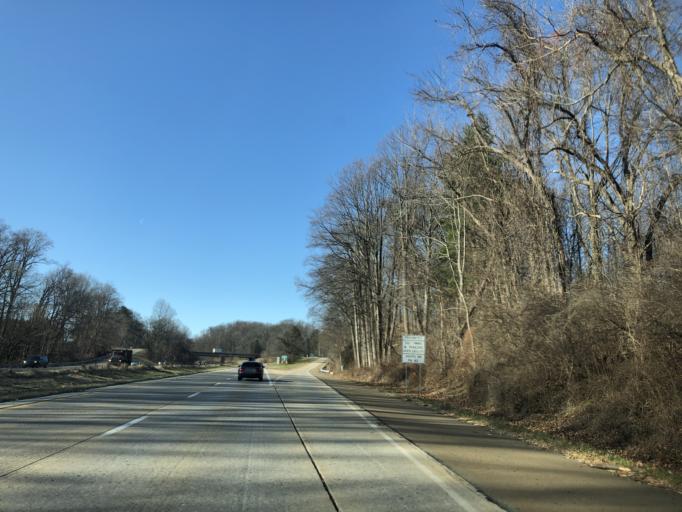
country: US
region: Pennsylvania
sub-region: Chester County
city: Kennett Square
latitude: 39.8565
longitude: -75.7104
